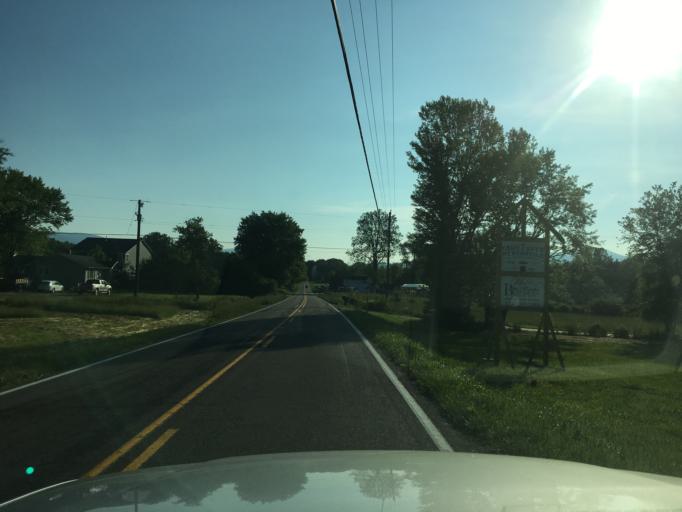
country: US
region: North Carolina
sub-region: Henderson County
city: Hoopers Creek
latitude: 35.4801
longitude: -82.4436
